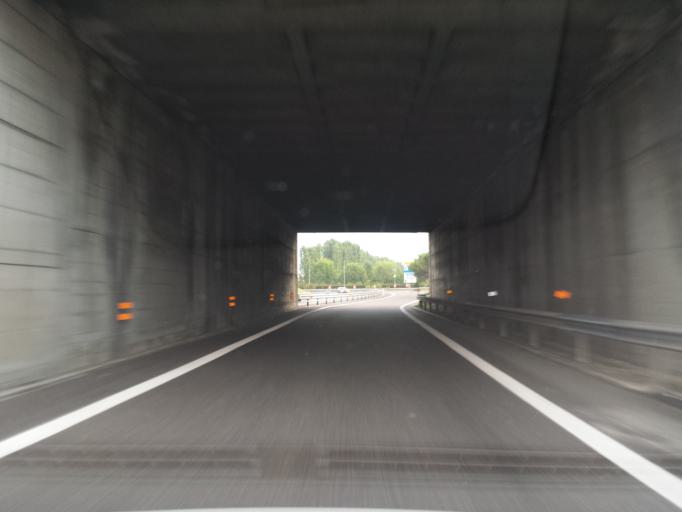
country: IT
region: Veneto
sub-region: Provincia di Padova
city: Vigodarzere
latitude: 45.4448
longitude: 11.8651
